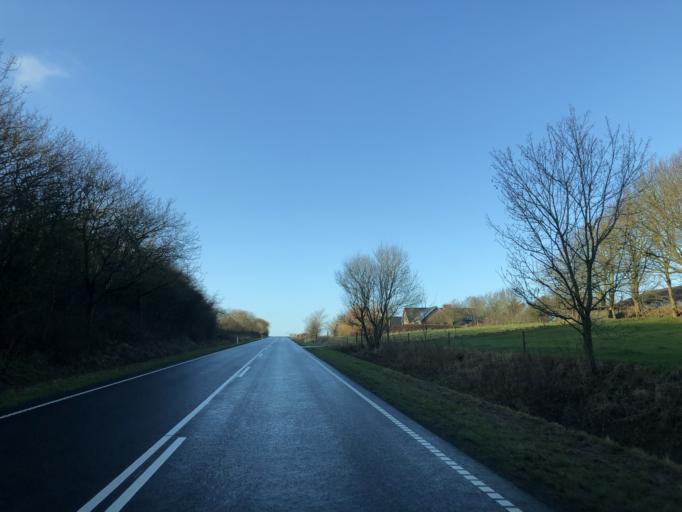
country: DK
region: Central Jutland
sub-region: Lemvig Kommune
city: Lemvig
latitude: 56.5588
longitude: 8.4321
